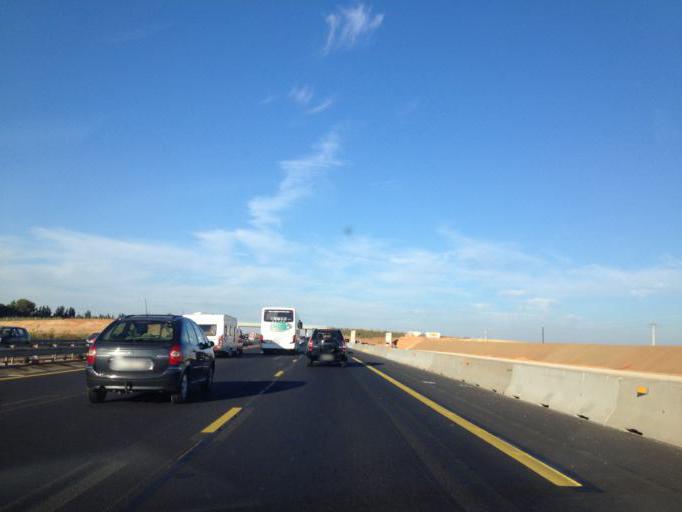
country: FR
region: Languedoc-Roussillon
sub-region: Departement de l'Herault
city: Saint-Aunes
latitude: 43.6285
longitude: 3.9656
